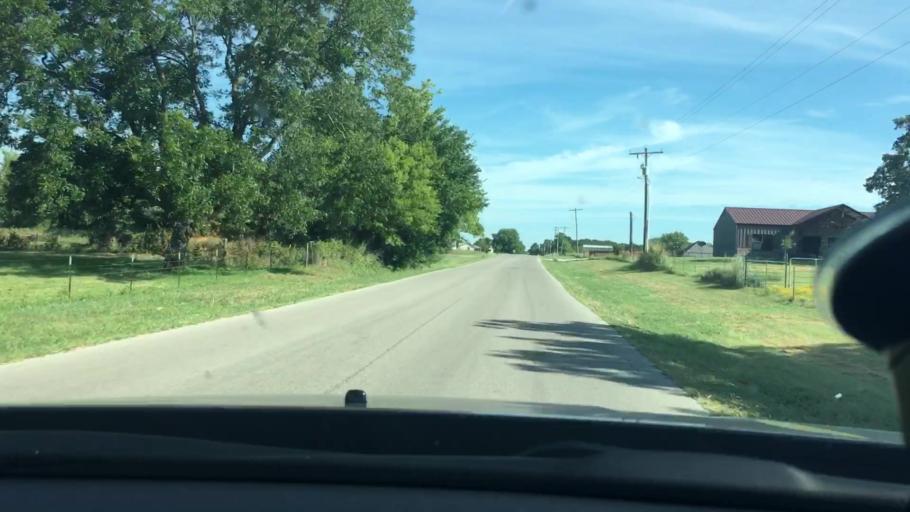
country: US
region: Oklahoma
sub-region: Carter County
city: Lone Grove
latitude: 34.2423
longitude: -97.2474
